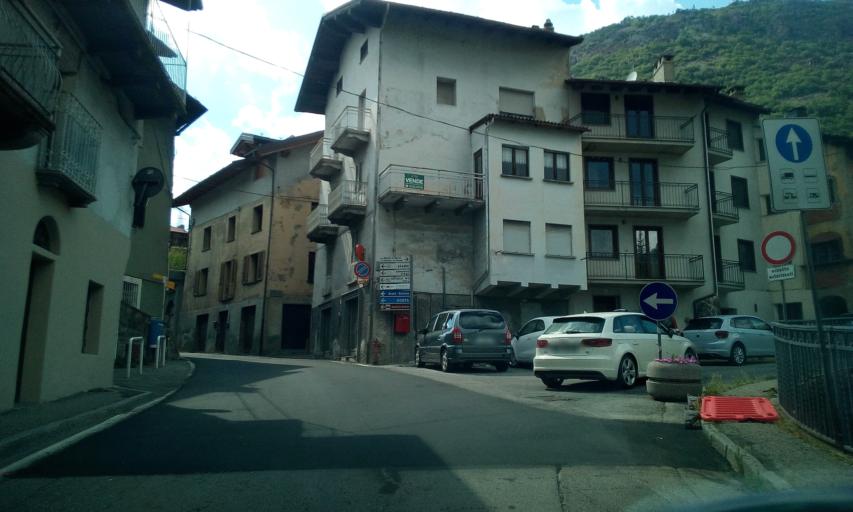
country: IT
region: Aosta Valley
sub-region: Valle d'Aosta
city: Chatillon
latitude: 45.7493
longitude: 7.6092
